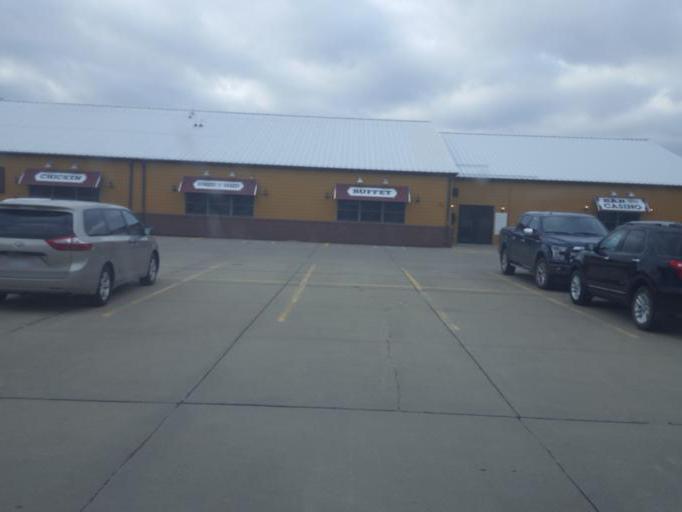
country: US
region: South Dakota
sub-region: Yankton County
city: Yankton
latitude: 42.9044
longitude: -97.3984
